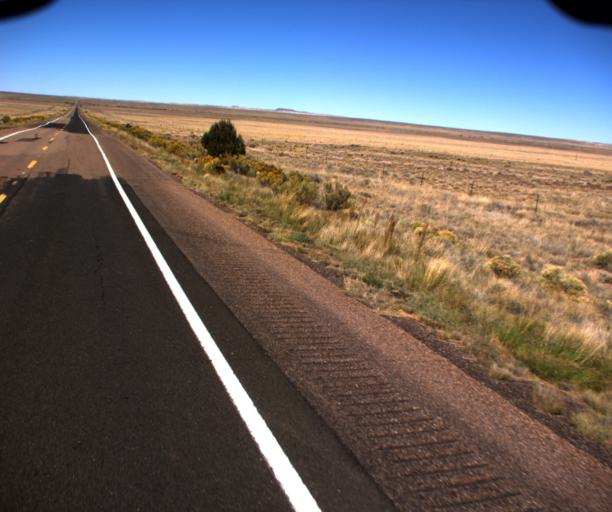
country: US
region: Arizona
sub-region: Navajo County
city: Snowflake
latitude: 34.7214
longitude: -109.7733
